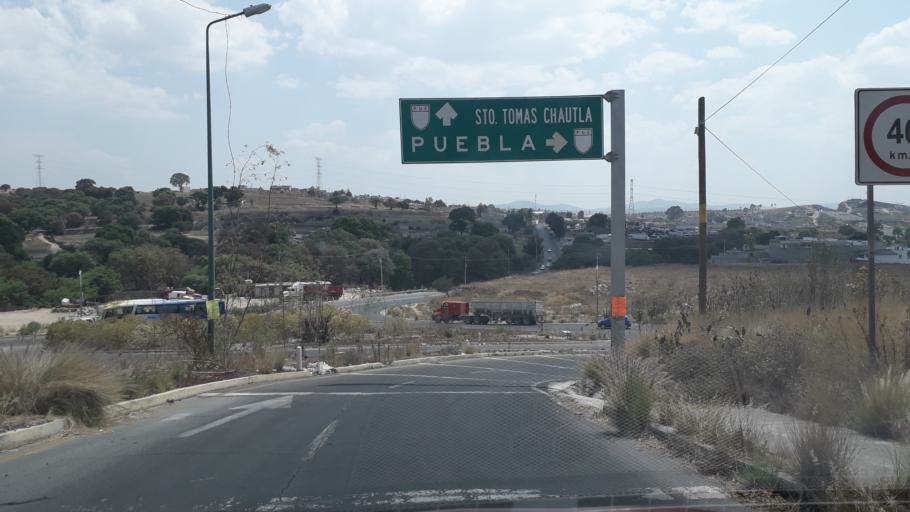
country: MX
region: Puebla
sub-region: Puebla
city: Galaxia la Calera
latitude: 18.9913
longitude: -98.1619
